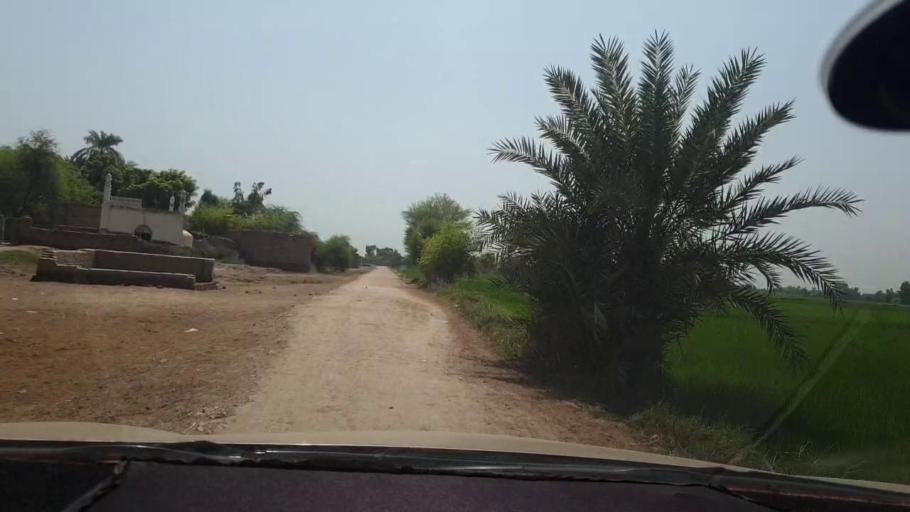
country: PK
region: Sindh
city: Kambar
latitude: 27.6374
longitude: 67.9337
